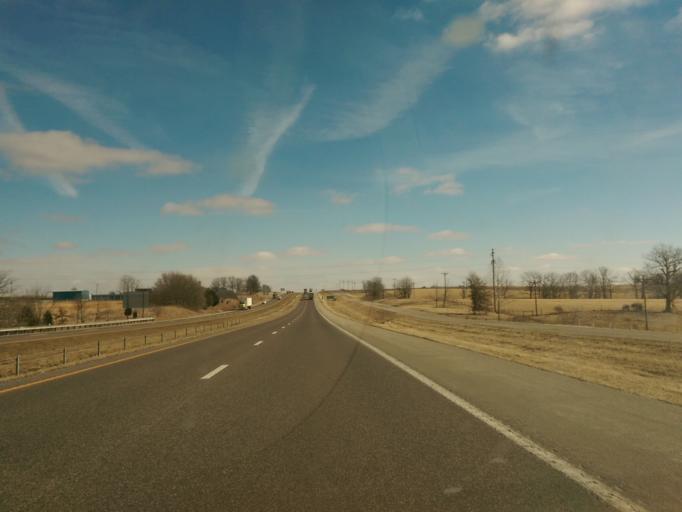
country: US
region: Missouri
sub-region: Callaway County
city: Fulton
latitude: 38.9441
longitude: -91.9274
